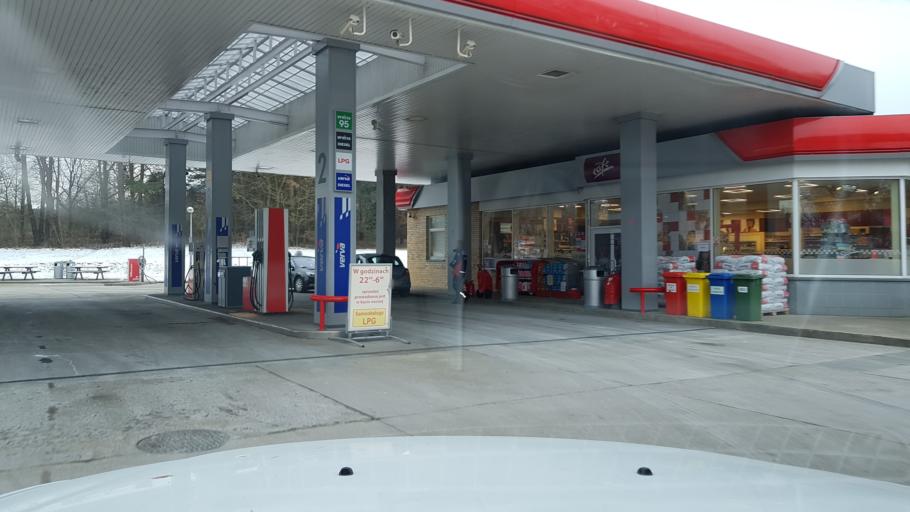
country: PL
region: West Pomeranian Voivodeship
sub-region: Powiat gryfinski
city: Widuchowa
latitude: 53.1142
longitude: 14.3992
